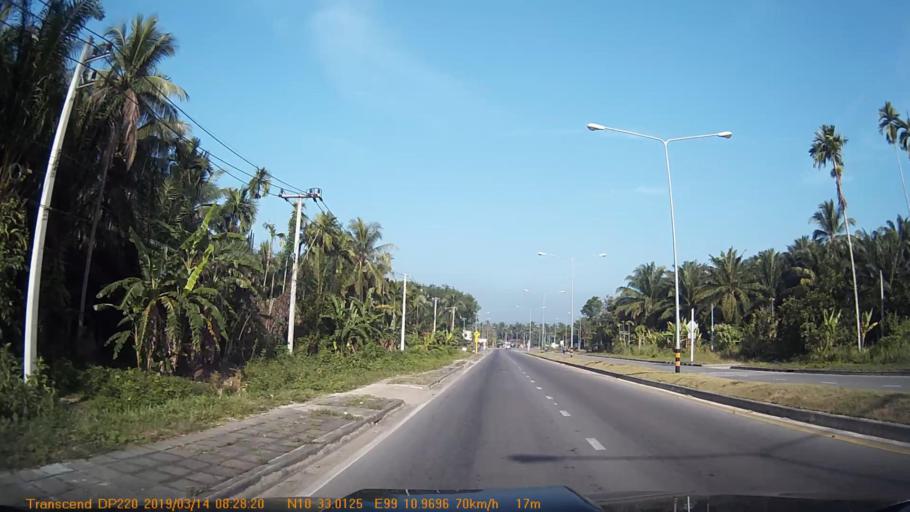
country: TH
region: Chumphon
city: Chumphon
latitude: 10.5503
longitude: 99.1826
